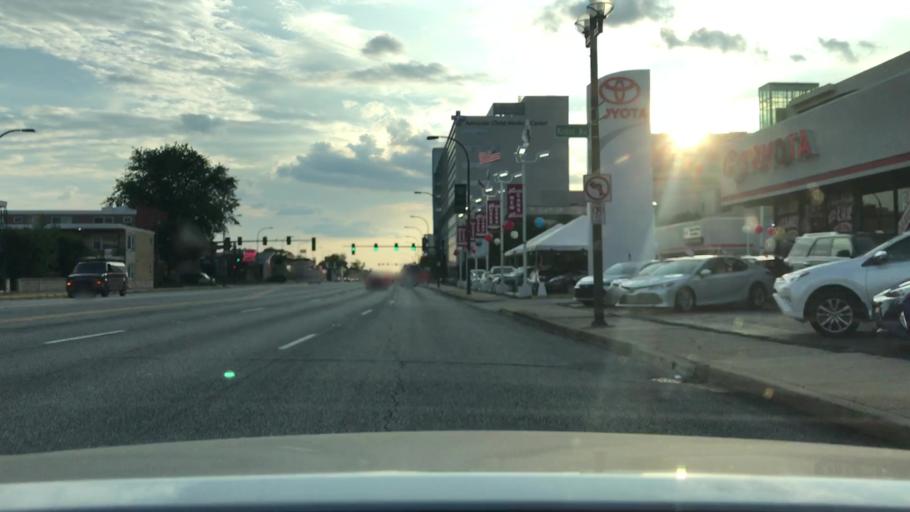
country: US
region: Illinois
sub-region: Cook County
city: Hometown
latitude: 41.7204
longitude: -87.7295
